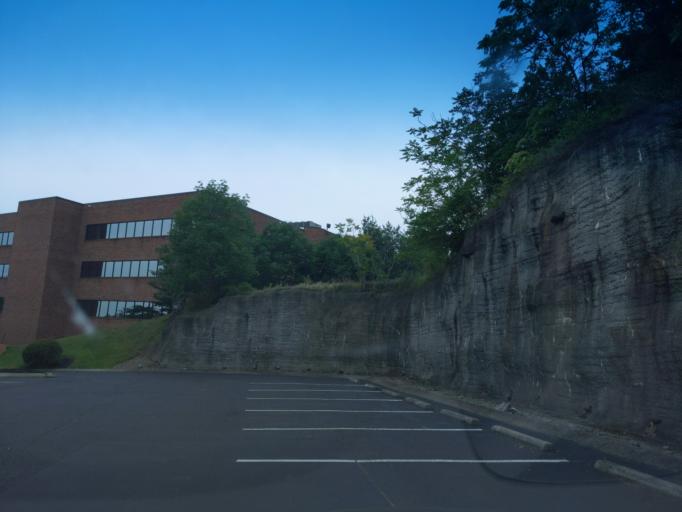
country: US
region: Tennessee
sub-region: Williamson County
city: Brentwood
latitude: 36.0386
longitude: -86.7803
